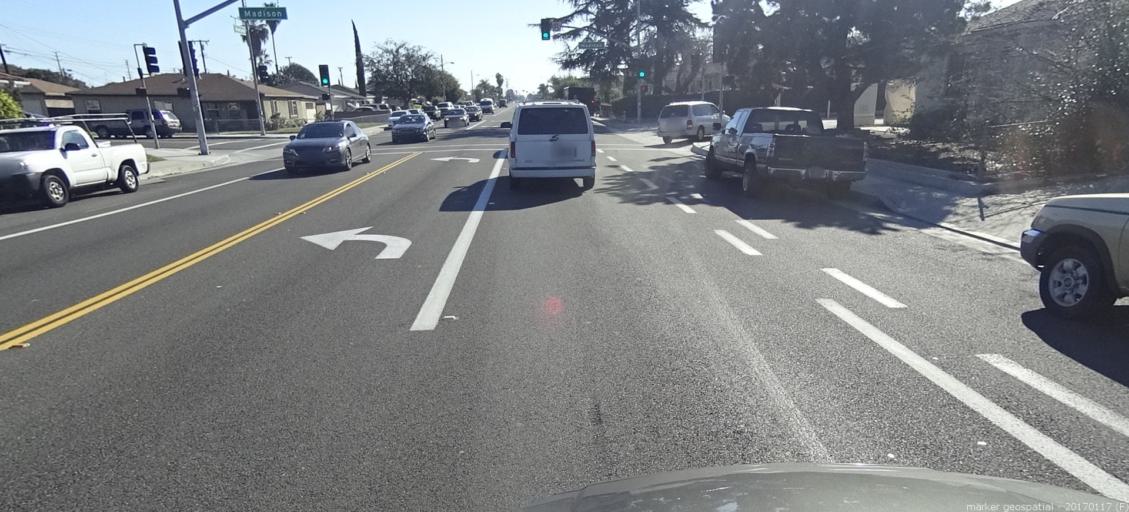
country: US
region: California
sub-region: Orange County
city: Midway City
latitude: 33.7489
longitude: -117.9810
